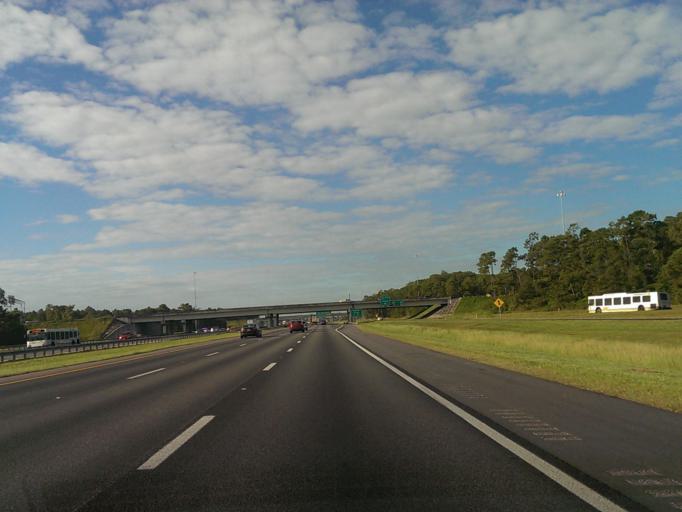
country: US
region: Florida
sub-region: Osceola County
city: Celebration
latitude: 28.3618
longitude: -81.5189
